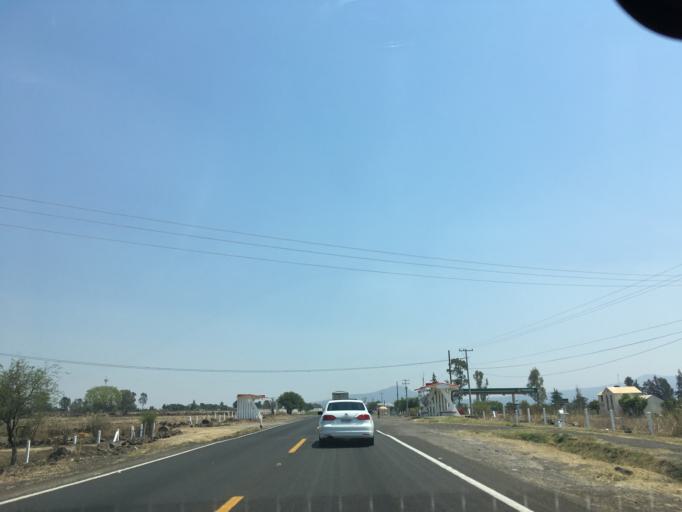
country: MX
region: Michoacan
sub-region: Cuitzeo
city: Cuamio
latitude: 20.0488
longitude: -101.1509
